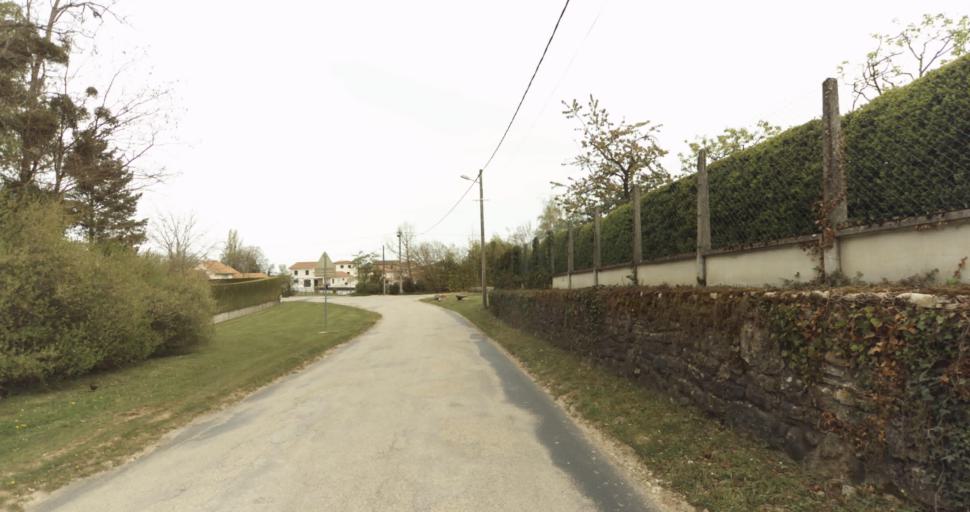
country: FR
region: Rhone-Alpes
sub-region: Departement de l'Ain
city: Amberieu-en-Bugey
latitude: 45.9637
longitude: 5.3667
